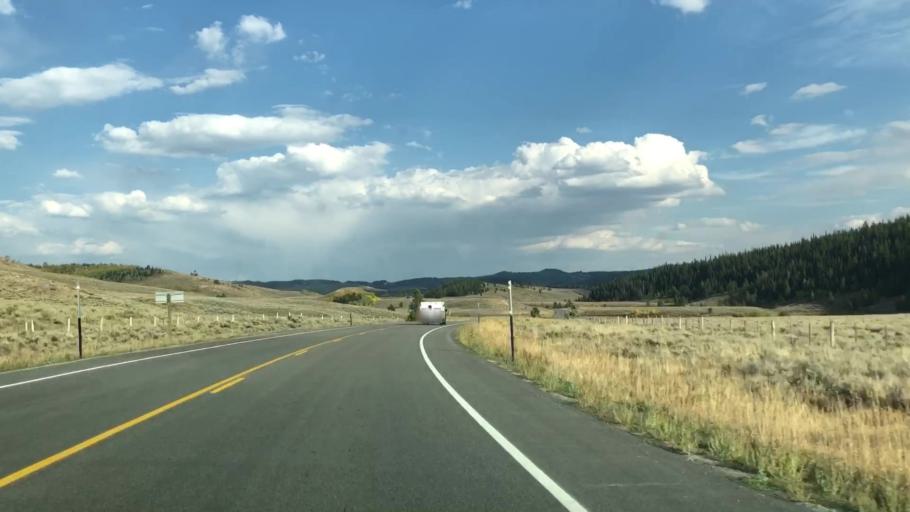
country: US
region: Wyoming
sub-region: Teton County
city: Hoback
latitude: 43.1554
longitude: -110.3004
